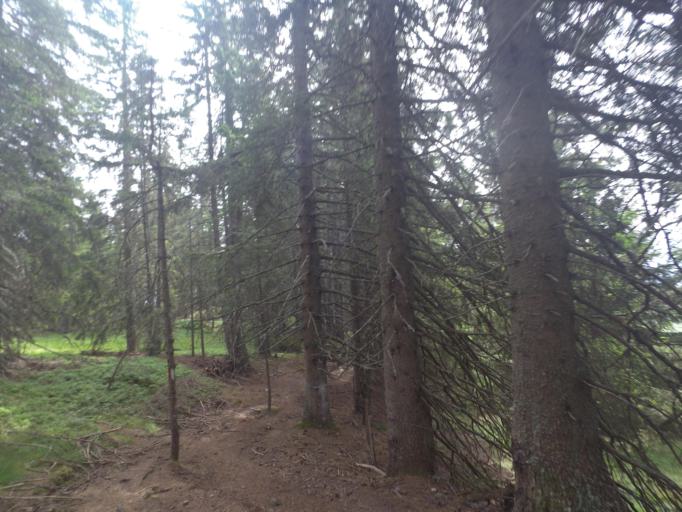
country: AT
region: Salzburg
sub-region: Politischer Bezirk Sankt Johann im Pongau
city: Muhlbach am Hochkonig
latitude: 47.3665
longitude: 13.0901
